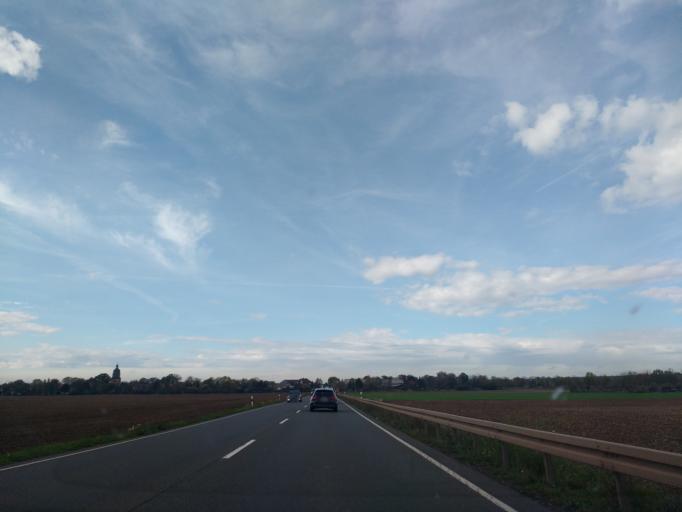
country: DE
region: Thuringia
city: Uthleben
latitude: 51.4822
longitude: 10.8550
